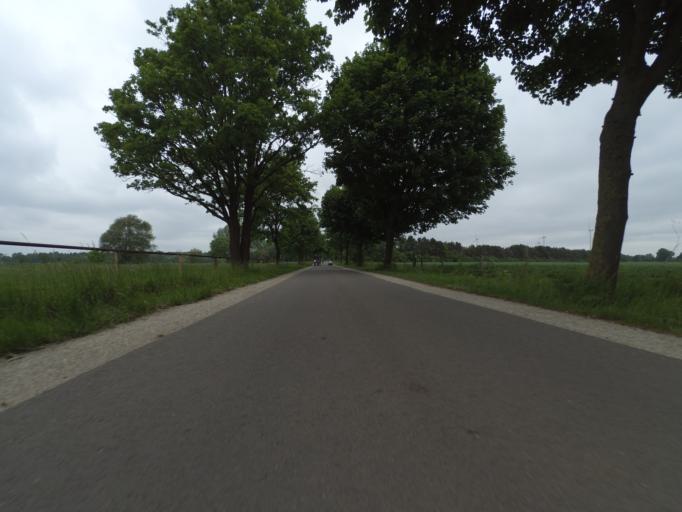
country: DE
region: Lower Saxony
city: Uetze
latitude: 52.4791
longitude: 10.2046
